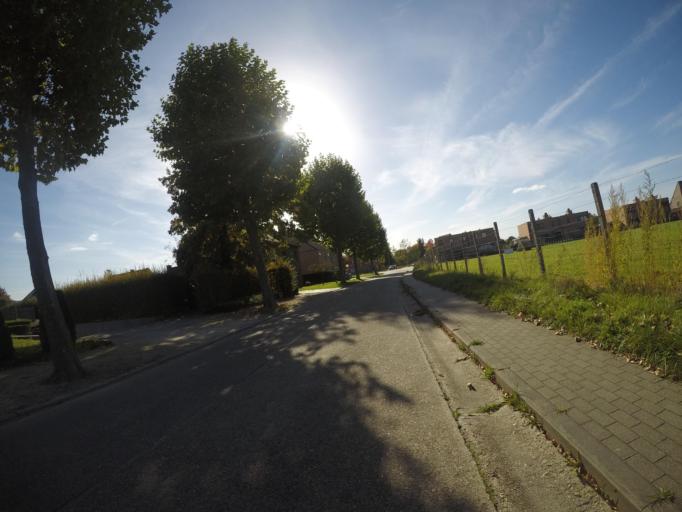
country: BE
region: Flanders
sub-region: Provincie Limburg
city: Diepenbeek
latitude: 50.9047
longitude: 5.4254
